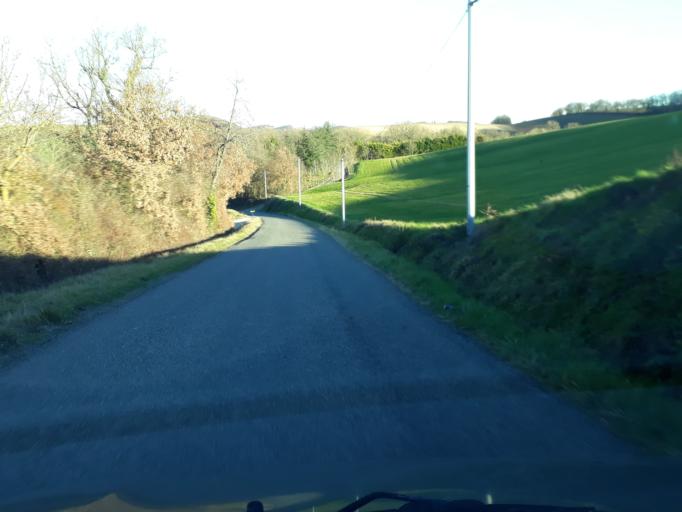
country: FR
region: Midi-Pyrenees
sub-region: Departement du Gers
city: Pavie
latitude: 43.6274
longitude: 0.6653
